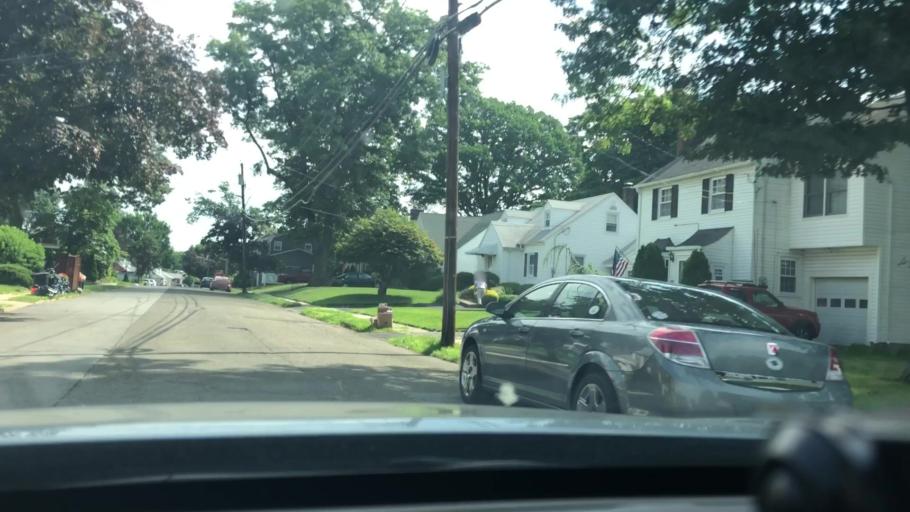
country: US
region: New Jersey
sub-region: Union County
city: Winfield
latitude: 40.6404
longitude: -74.2756
